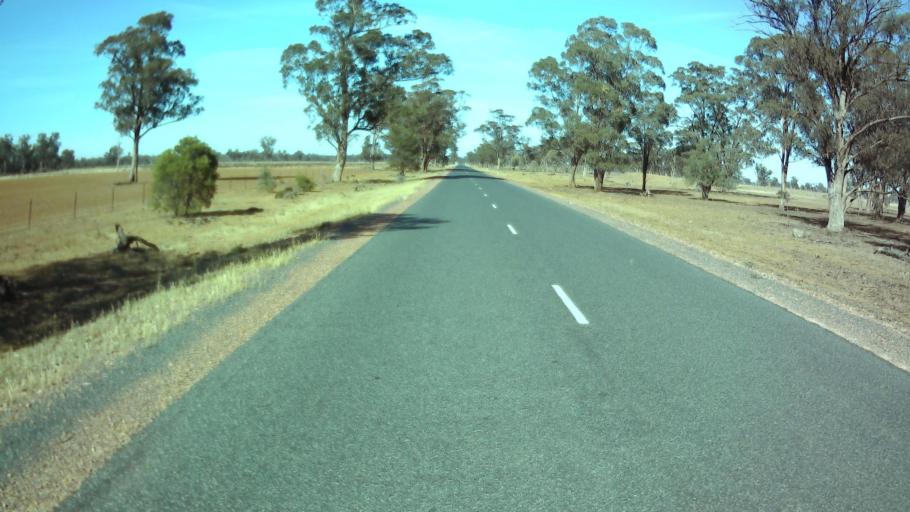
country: AU
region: New South Wales
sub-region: Weddin
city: Grenfell
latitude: -34.1028
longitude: 147.8713
